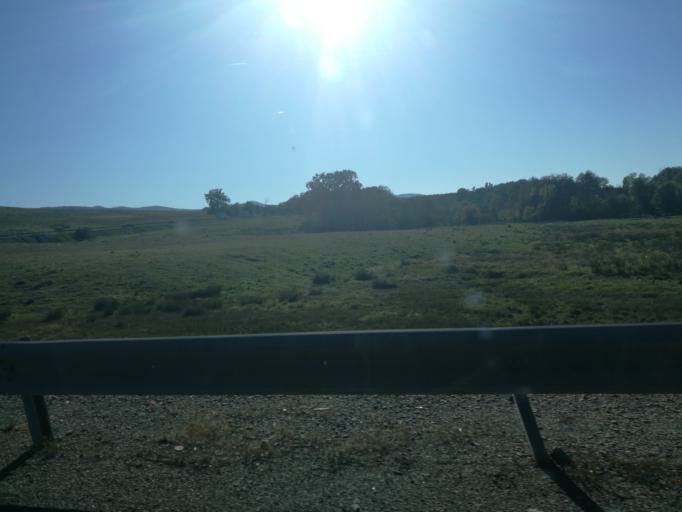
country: RO
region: Brasov
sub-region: Comuna Dumbravita
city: Dumbravita
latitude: 45.7574
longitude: 25.4000
